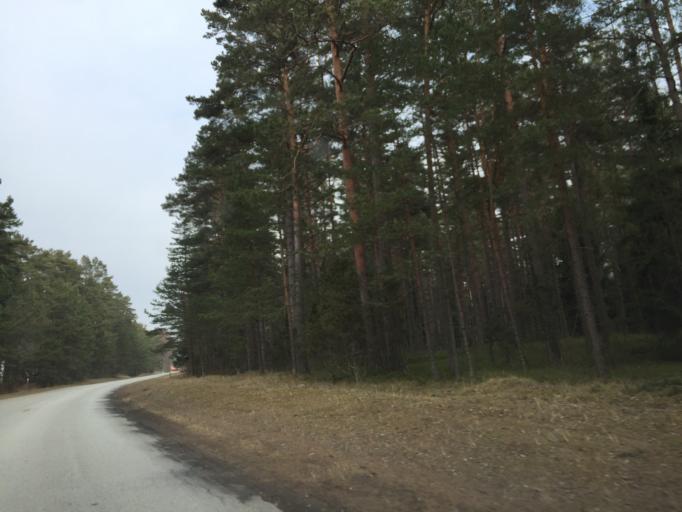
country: LV
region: Salacgrivas
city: Ainazi
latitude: 57.9491
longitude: 24.3915
